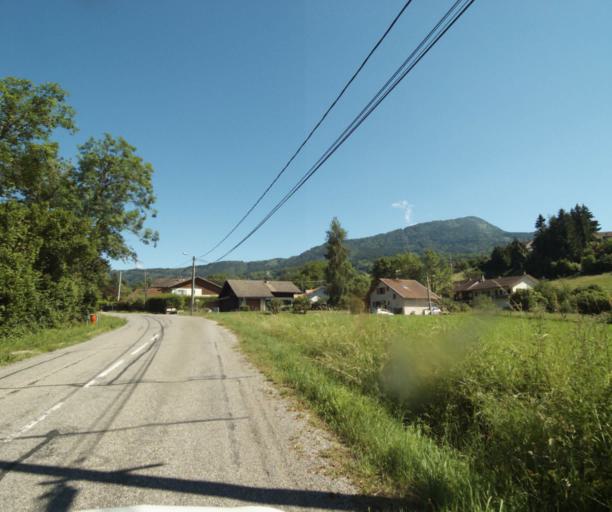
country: FR
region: Rhone-Alpes
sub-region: Departement de la Haute-Savoie
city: Bons-en-Chablais
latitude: 46.2629
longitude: 6.3534
